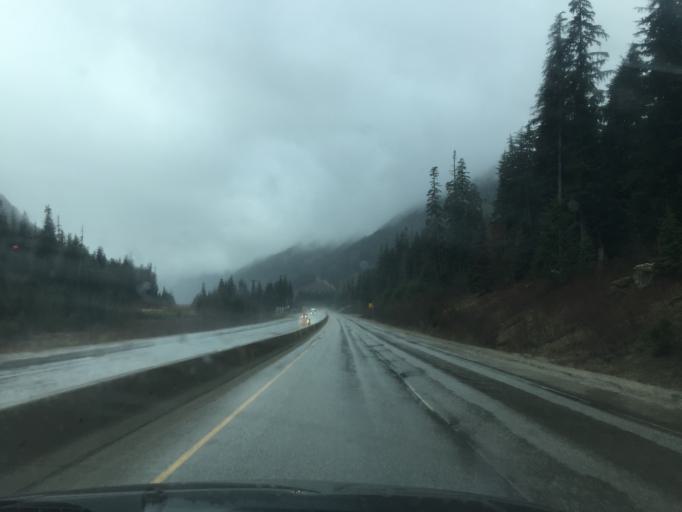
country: CA
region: British Columbia
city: Hope
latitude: 49.5804
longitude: -121.1743
